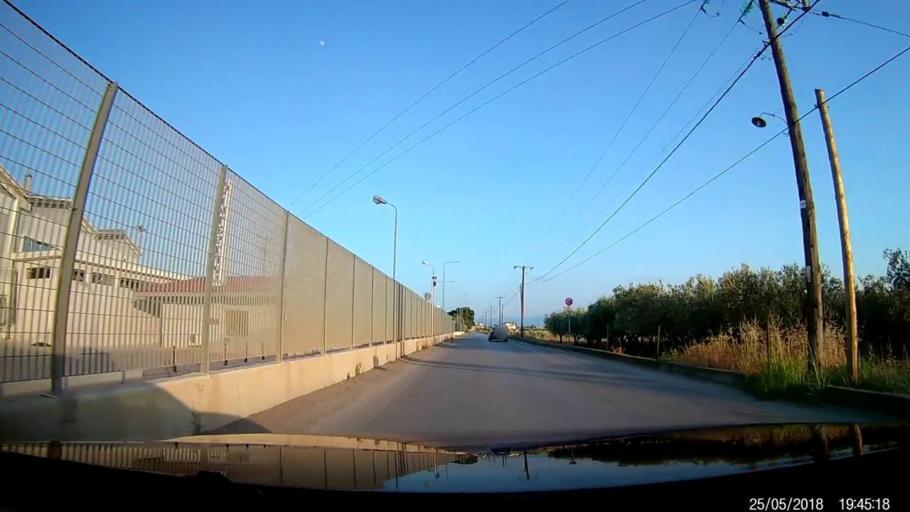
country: GR
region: Central Greece
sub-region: Nomos Evvoias
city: Ayios Nikolaos
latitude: 38.4342
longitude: 23.6324
